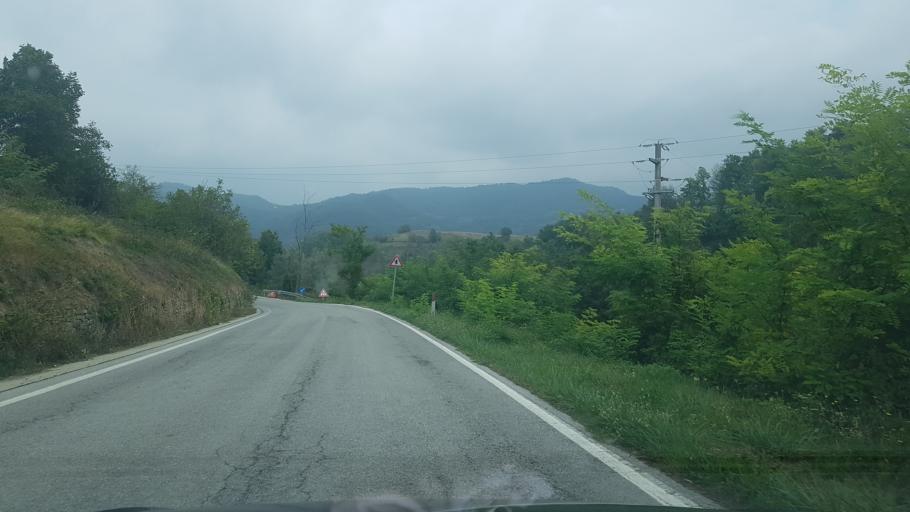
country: IT
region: Piedmont
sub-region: Provincia di Cuneo
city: Camerana
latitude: 44.4277
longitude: 8.1442
